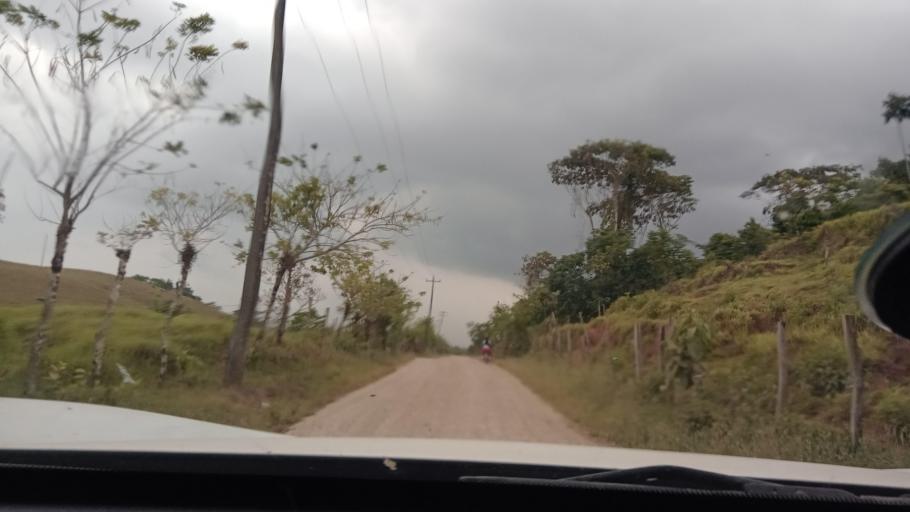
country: MX
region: Tabasco
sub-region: Huimanguillo
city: Francisco Rueda
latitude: 17.4350
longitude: -94.0524
